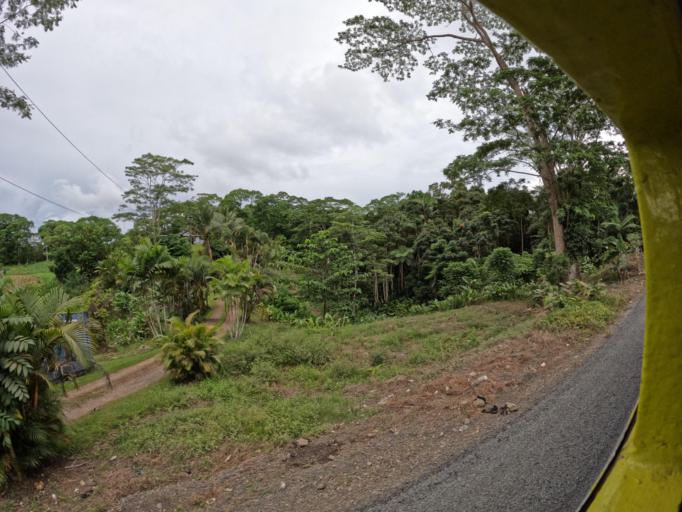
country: FJ
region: Central
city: Suva
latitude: -18.0681
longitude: 178.4611
